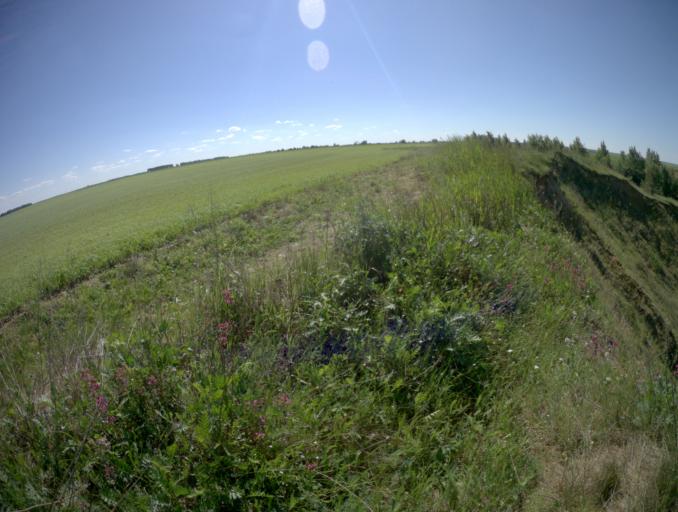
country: RU
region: Ivanovo
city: Gavrilov Posad
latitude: 56.5309
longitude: 40.2015
